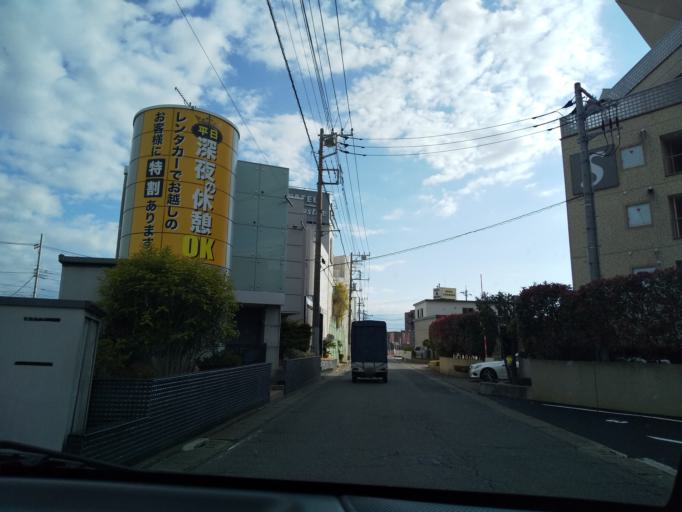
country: JP
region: Tokyo
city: Hino
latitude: 35.6724
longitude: 139.4427
